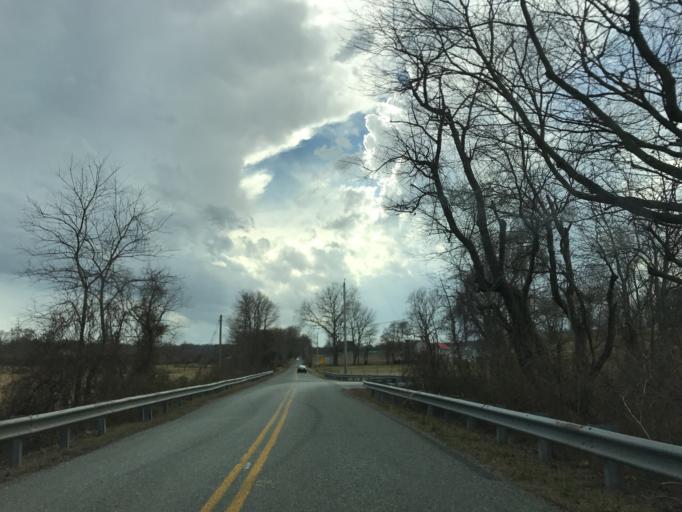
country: US
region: Maryland
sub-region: Harford County
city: South Bel Air
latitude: 39.5931
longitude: -76.2877
